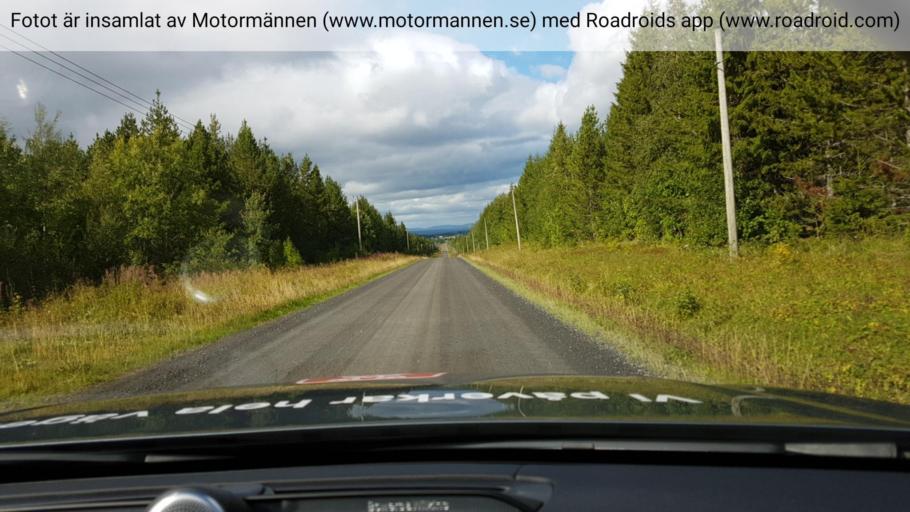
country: SE
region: Jaemtland
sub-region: OEstersunds Kommun
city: Lit
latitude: 63.6175
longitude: 14.9841
